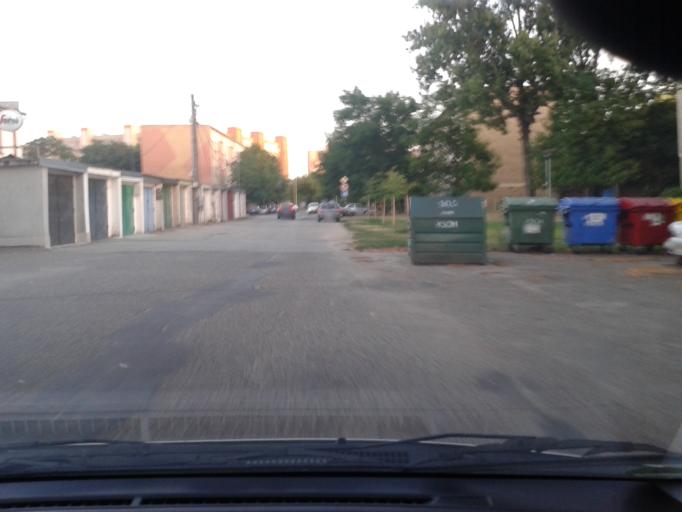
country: SK
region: Nitriansky
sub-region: Okres Nove Zamky
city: Sturovo
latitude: 47.7941
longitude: 18.7203
